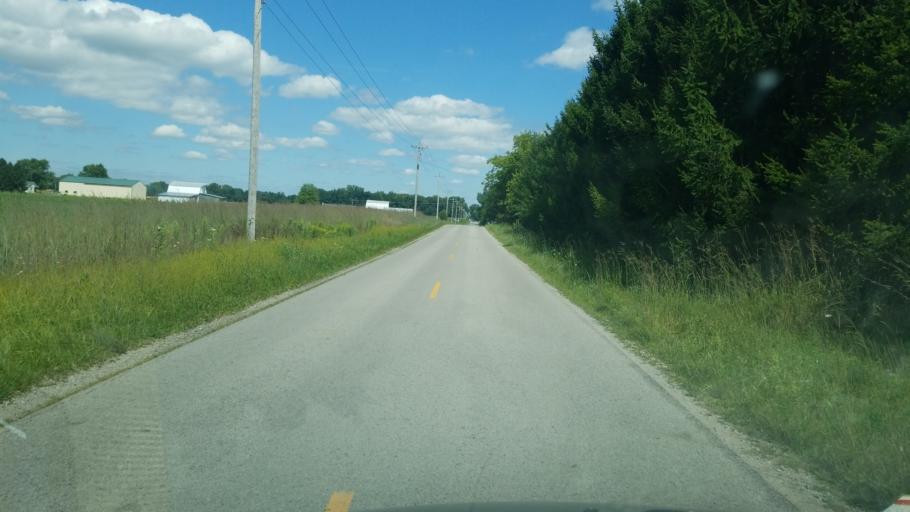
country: US
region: Ohio
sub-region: Henry County
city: Liberty Center
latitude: 41.4836
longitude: -83.9413
